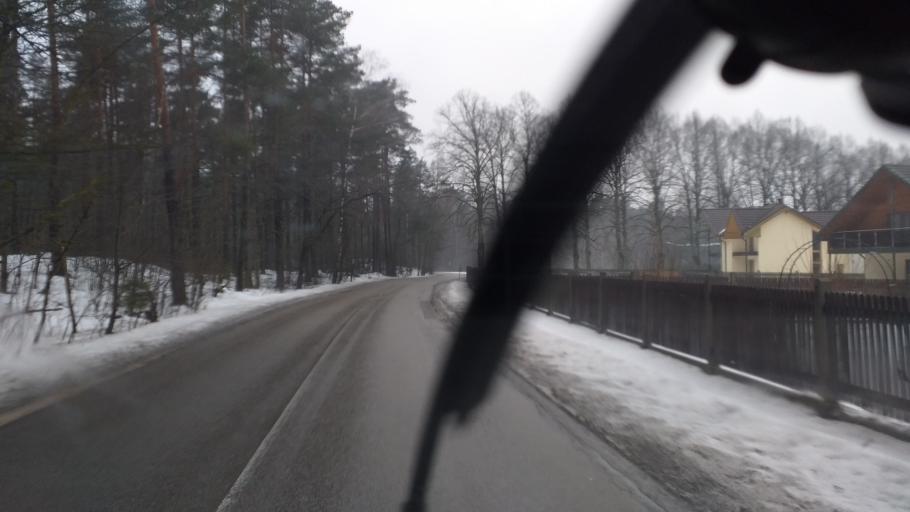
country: LV
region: Riga
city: Daugavgriva
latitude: 56.9814
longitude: 23.9914
